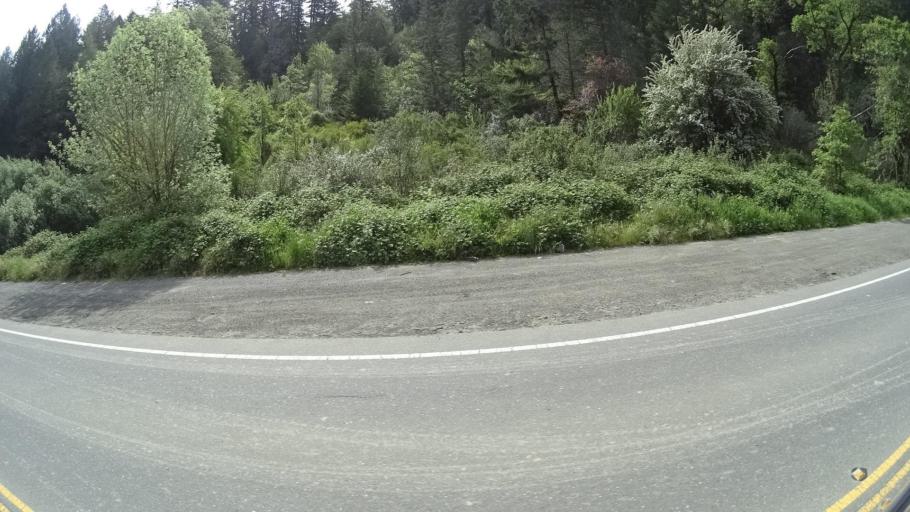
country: US
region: California
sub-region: Humboldt County
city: Redway
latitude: 40.1390
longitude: -123.8126
